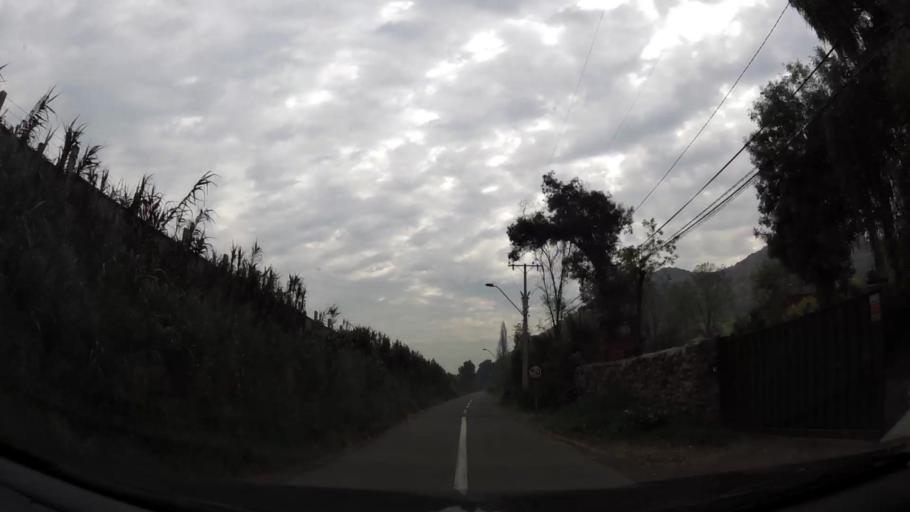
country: CL
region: Santiago Metropolitan
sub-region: Provincia de Chacabuco
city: Chicureo Abajo
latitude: -33.2442
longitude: -70.6751
